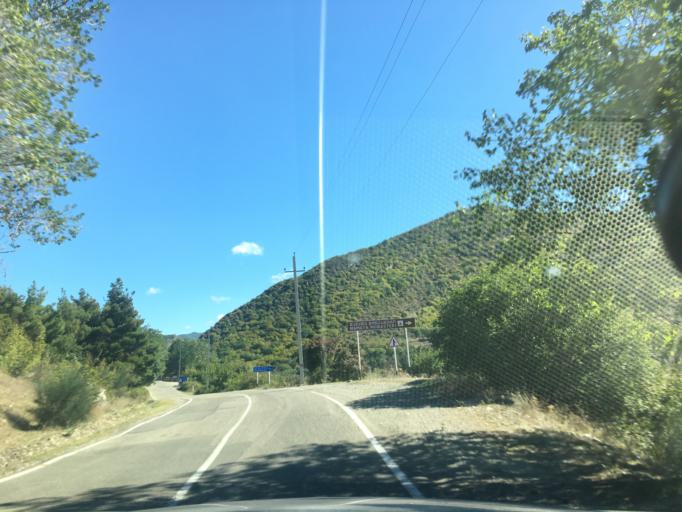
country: GE
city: Zahesi
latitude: 41.8325
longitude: 44.8622
